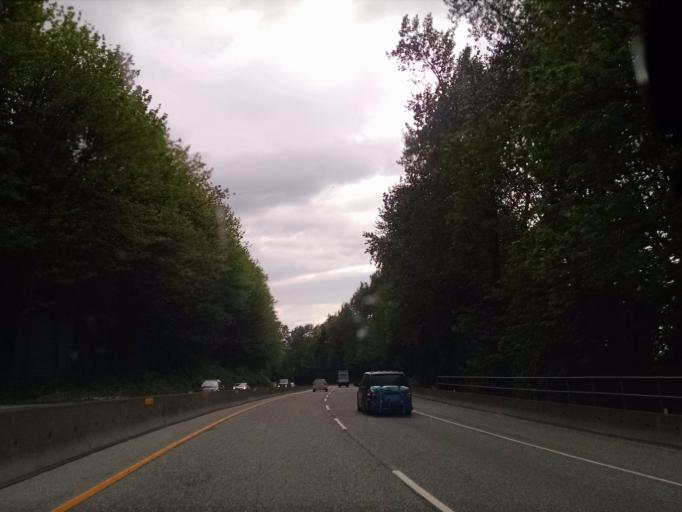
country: CA
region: British Columbia
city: Agassiz
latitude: 49.1724
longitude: -121.7780
